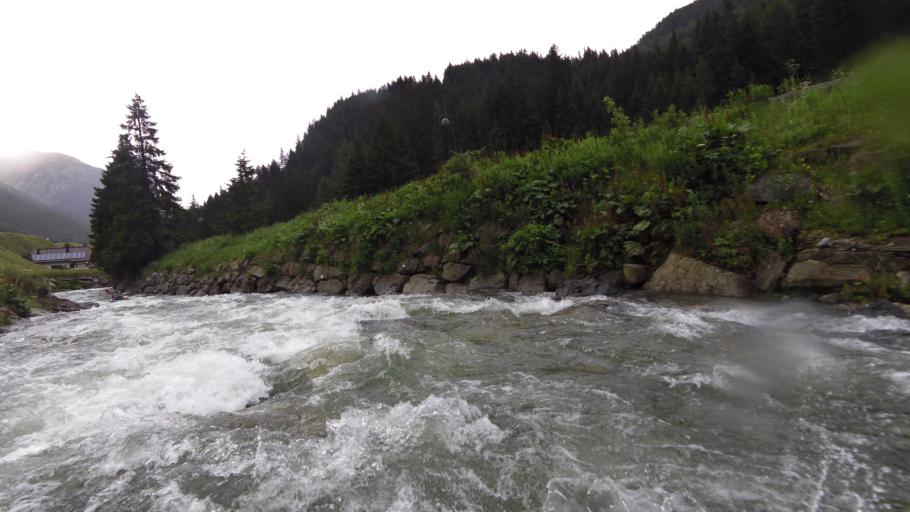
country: AT
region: Tyrol
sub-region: Politischer Bezirk Landeck
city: Galtur
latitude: 46.9766
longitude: 10.2110
